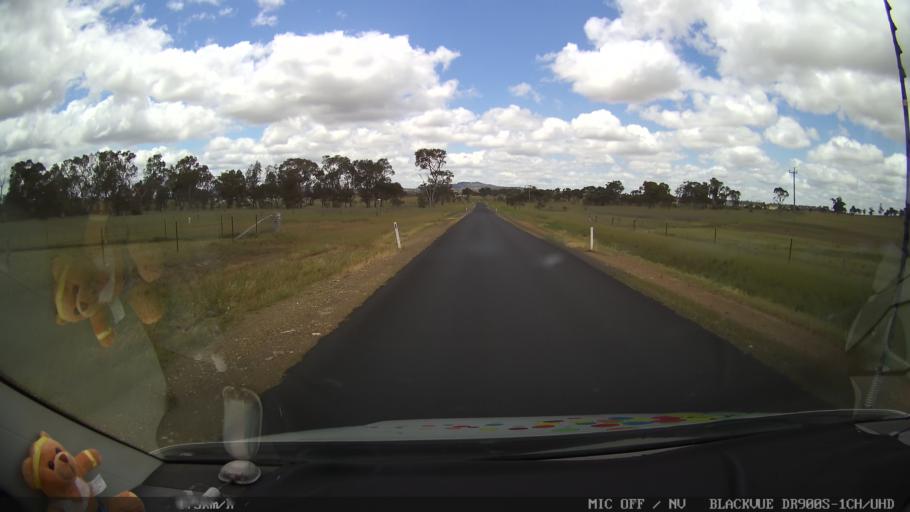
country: AU
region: New South Wales
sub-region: Glen Innes Severn
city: Glen Innes
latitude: -29.4386
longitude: 151.8333
